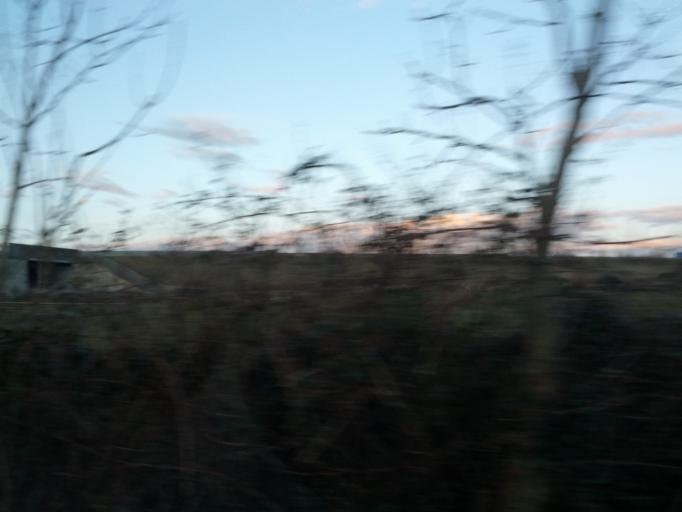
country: IE
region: Connaught
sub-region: County Galway
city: Athenry
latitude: 53.2817
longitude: -8.7525
